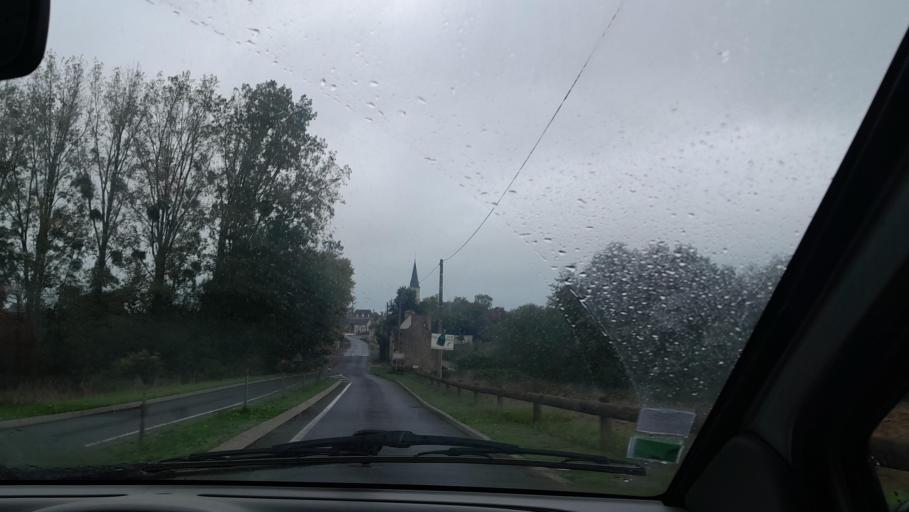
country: FR
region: Pays de la Loire
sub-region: Departement de la Mayenne
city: Congrier
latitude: 47.8763
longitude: -1.1287
